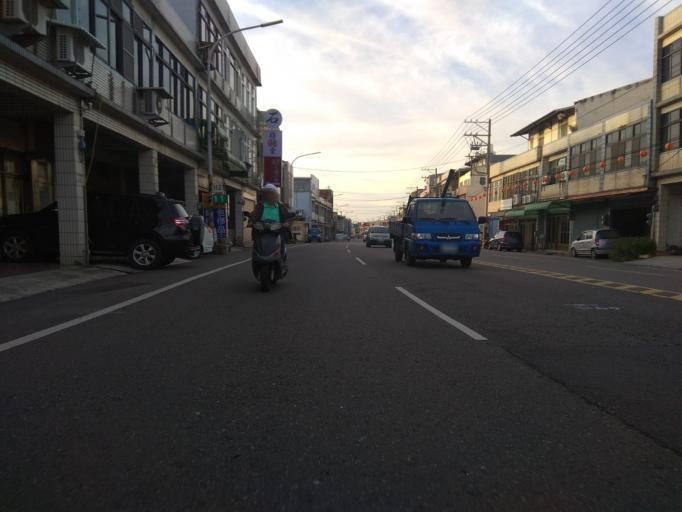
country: TW
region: Taiwan
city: Taoyuan City
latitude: 24.9958
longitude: 121.1634
